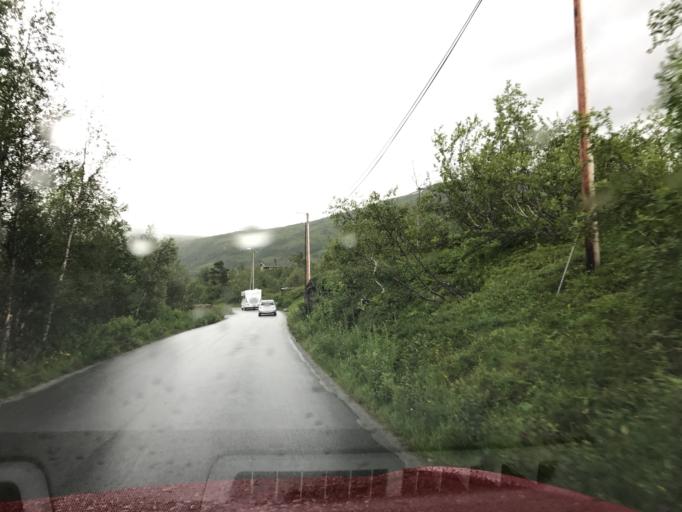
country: NO
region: Hordaland
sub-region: Eidfjord
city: Eidfjord
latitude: 60.4250
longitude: 7.2590
